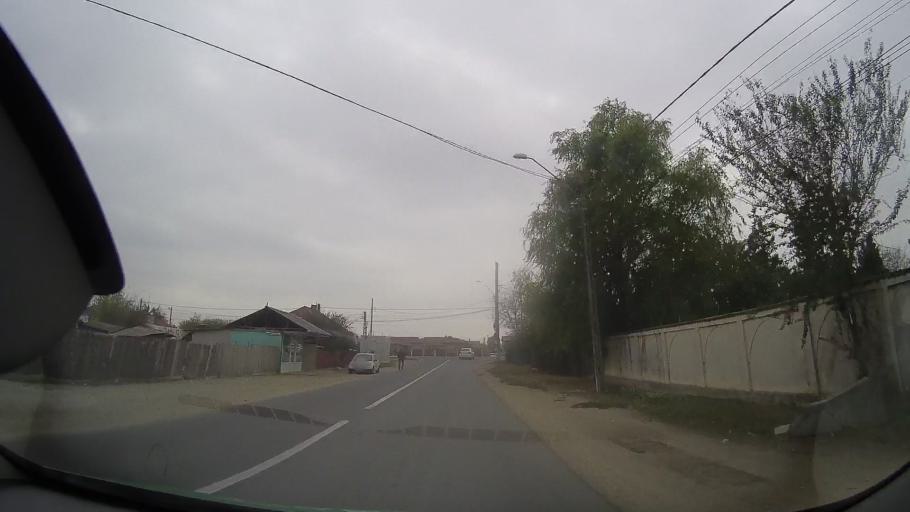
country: RO
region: Ialomita
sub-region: Comuna Manasia
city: Manasia
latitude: 44.7073
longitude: 26.6712
